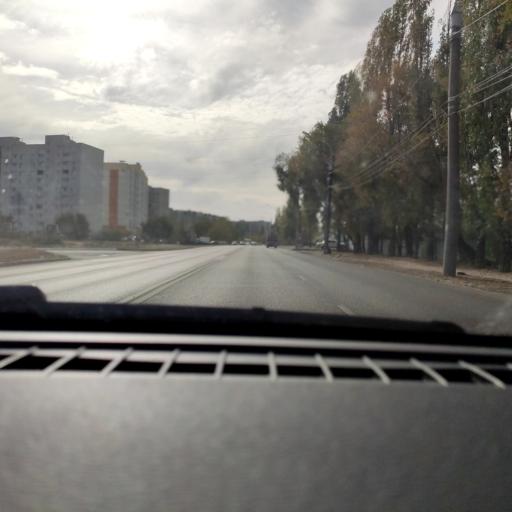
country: RU
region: Voronezj
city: Voronezh
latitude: 51.6469
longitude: 39.2674
